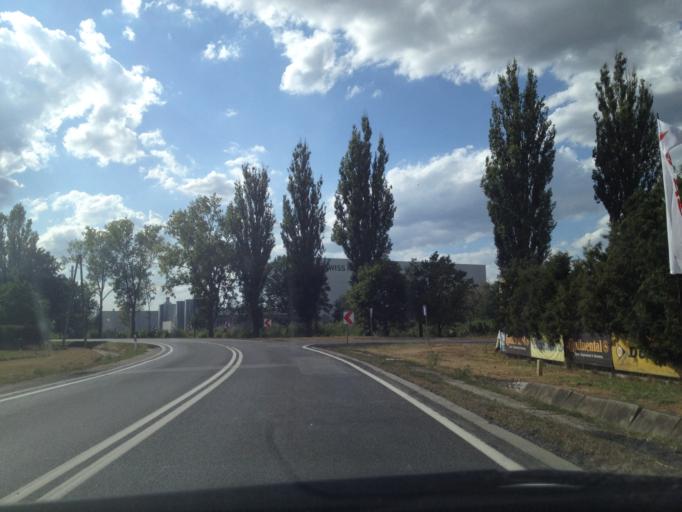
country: PL
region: Lubusz
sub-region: Powiat zarski
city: Zary
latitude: 51.6345
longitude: 15.1137
